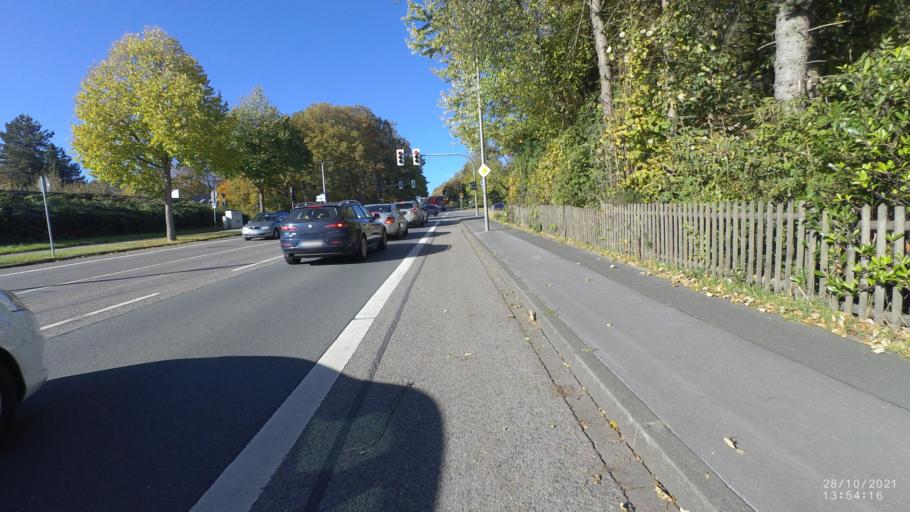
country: DE
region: North Rhine-Westphalia
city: Iserlohn
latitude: 51.3911
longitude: 7.6698
